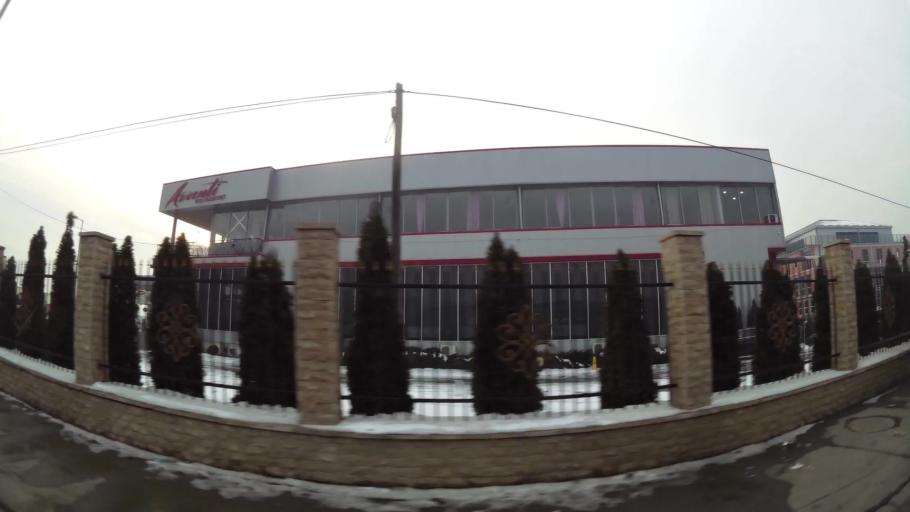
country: MK
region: Suto Orizari
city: Suto Orizare
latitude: 42.0258
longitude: 21.4296
